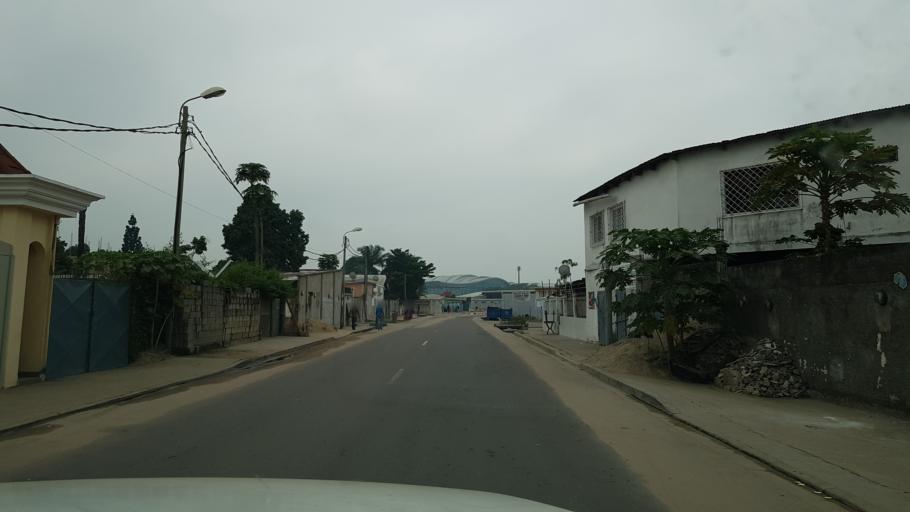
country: CG
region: Brazzaville
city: Brazzaville
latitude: -4.2582
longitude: 15.2576
